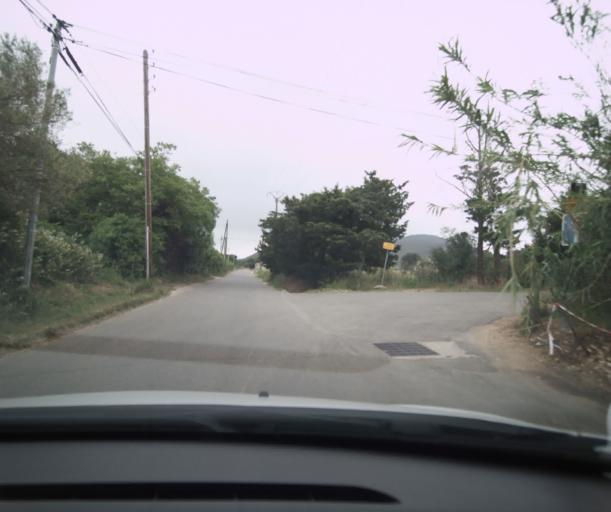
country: FR
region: Provence-Alpes-Cote d'Azur
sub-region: Departement du Var
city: Carqueiranne
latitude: 43.1217
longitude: 6.0505
